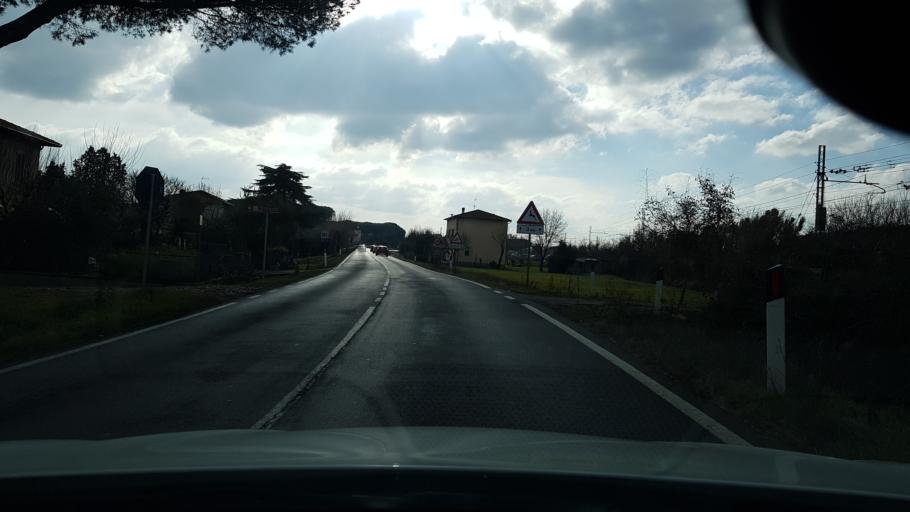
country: IT
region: Umbria
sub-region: Provincia di Perugia
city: Castiglione del Lago
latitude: 43.1551
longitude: 12.0186
